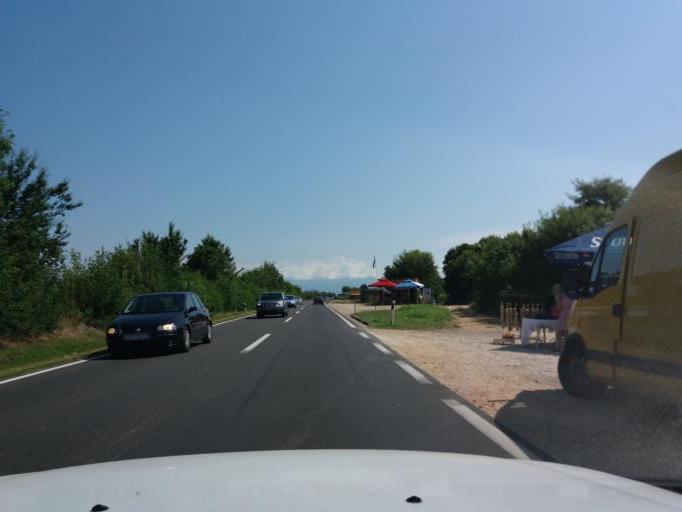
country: HR
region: Zadarska
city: Policnik
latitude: 44.1541
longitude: 15.3362
